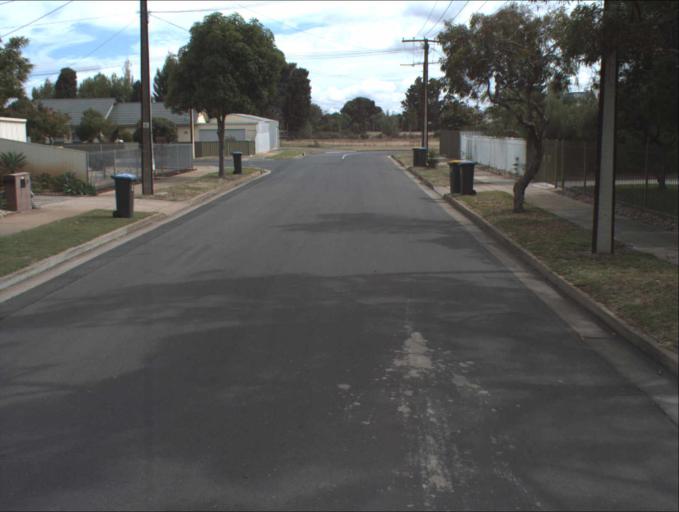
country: AU
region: South Australia
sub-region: Port Adelaide Enfield
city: Birkenhead
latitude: -34.8150
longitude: 138.5036
